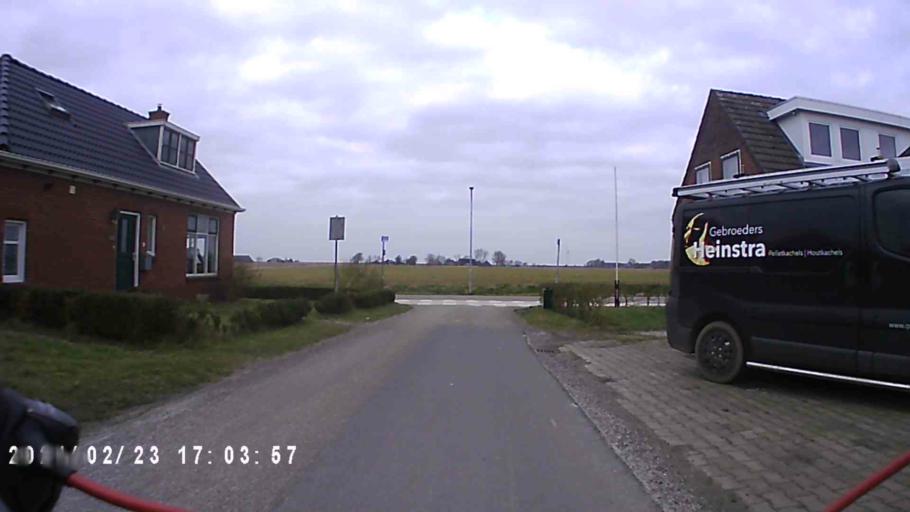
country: NL
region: Groningen
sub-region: Gemeente De Marne
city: Ulrum
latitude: 53.3876
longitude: 6.3842
